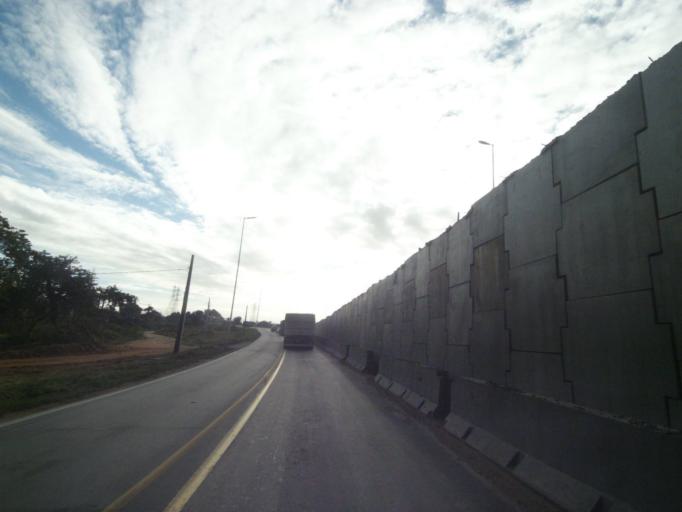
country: BR
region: Parana
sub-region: Paranagua
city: Paranagua
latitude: -25.5554
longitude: -48.5638
